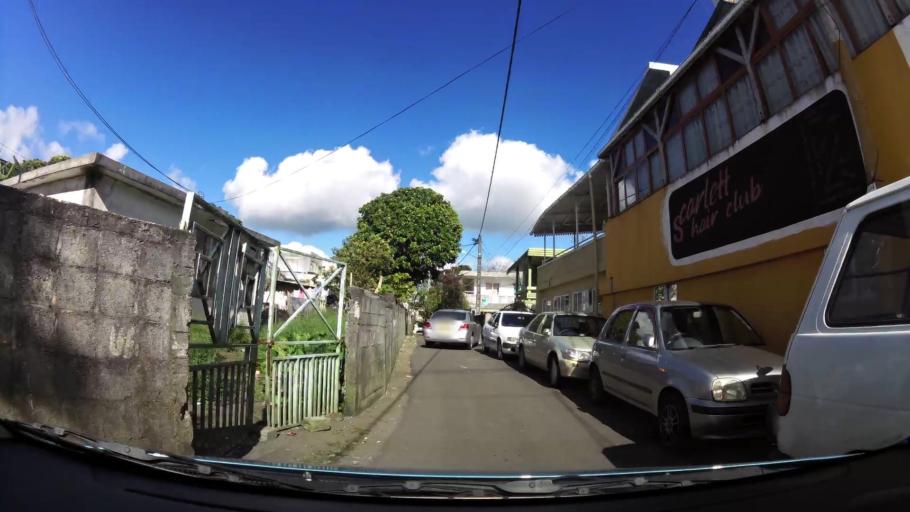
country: MU
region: Plaines Wilhems
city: Curepipe
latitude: -20.2961
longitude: 57.5173
